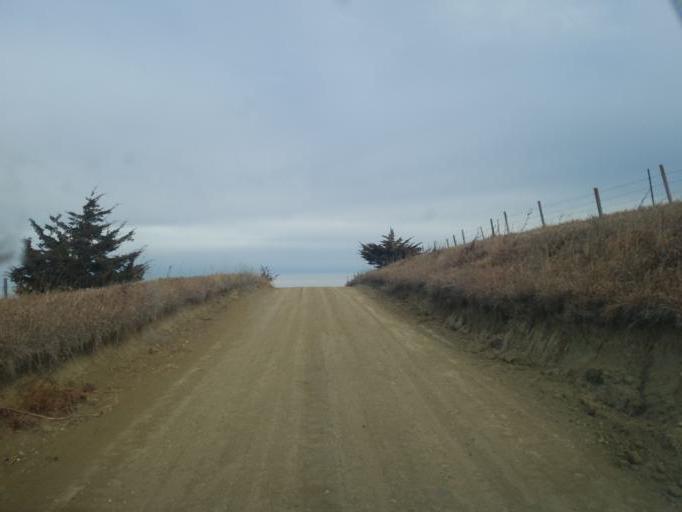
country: US
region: Nebraska
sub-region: Knox County
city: Center
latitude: 42.5985
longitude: -97.8379
